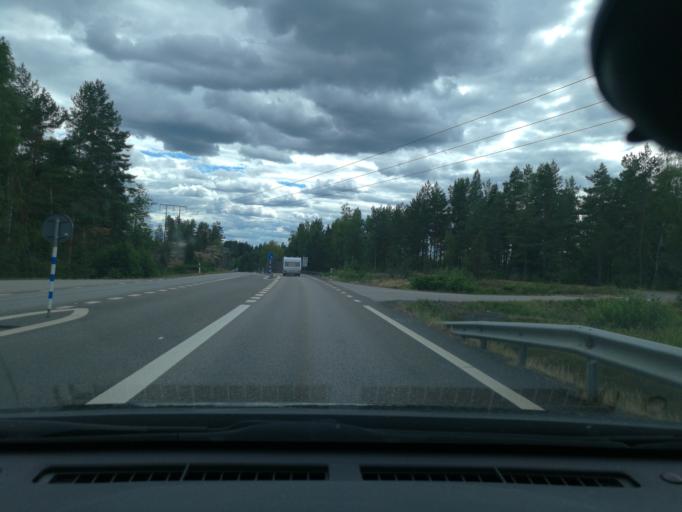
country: SE
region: OEstergoetland
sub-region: Valdemarsviks Kommun
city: Valdemarsvik
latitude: 58.0932
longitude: 16.5255
